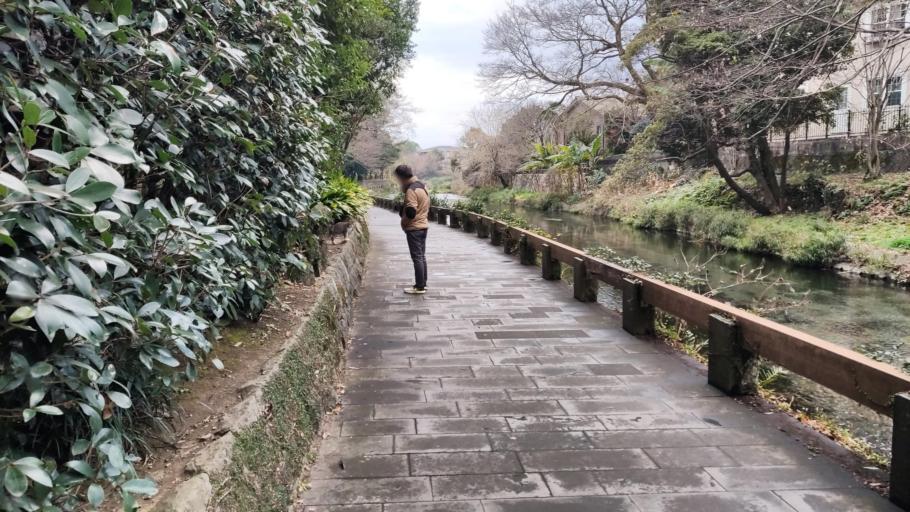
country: JP
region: Kumamoto
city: Kumamoto
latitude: 32.7867
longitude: 130.7346
